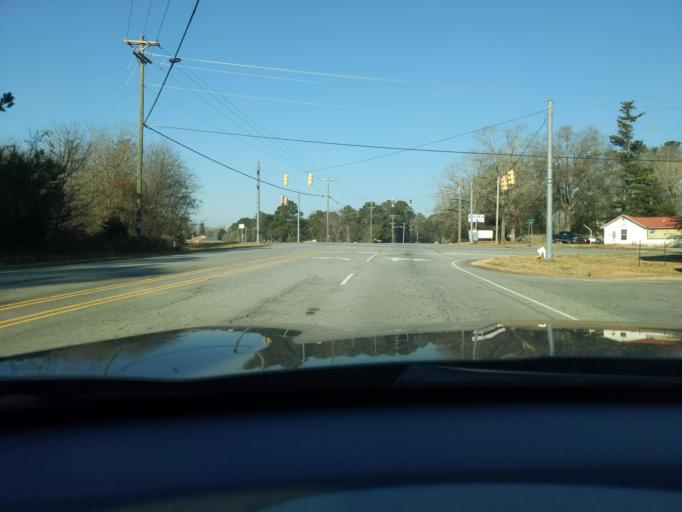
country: US
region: South Carolina
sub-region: Greenwood County
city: Greenwood
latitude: 34.1831
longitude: -82.1081
